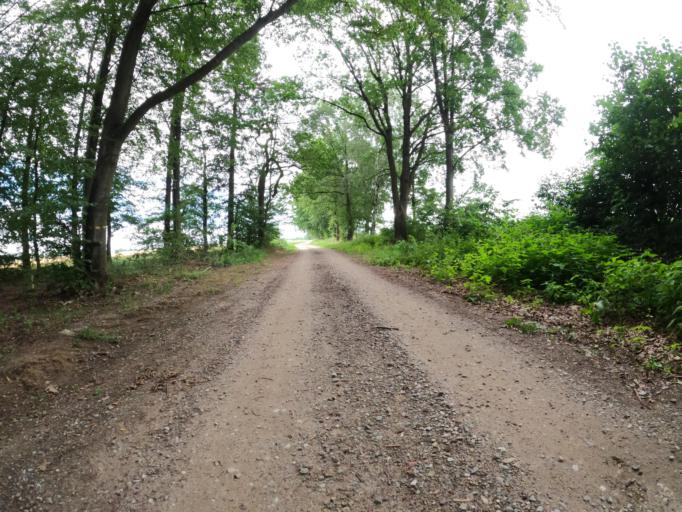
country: PL
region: West Pomeranian Voivodeship
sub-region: Powiat bialogardzki
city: Tychowo
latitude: 53.9939
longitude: 16.3799
